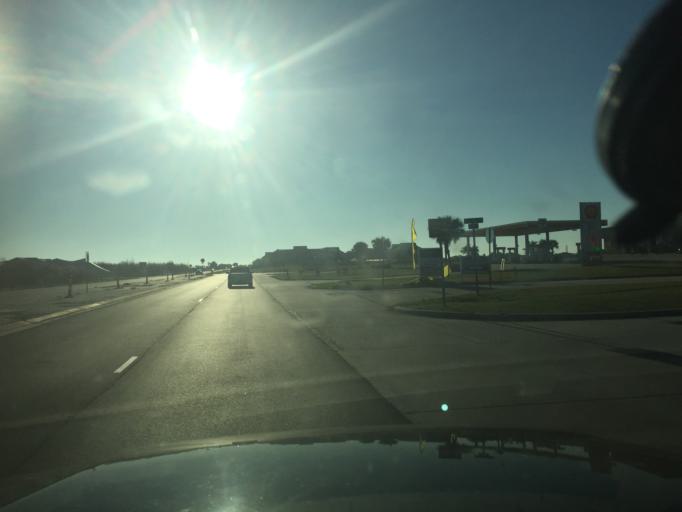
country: US
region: Louisiana
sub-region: Saint Tammany Parish
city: Eden Isle
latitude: 30.2198
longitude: -89.7806
